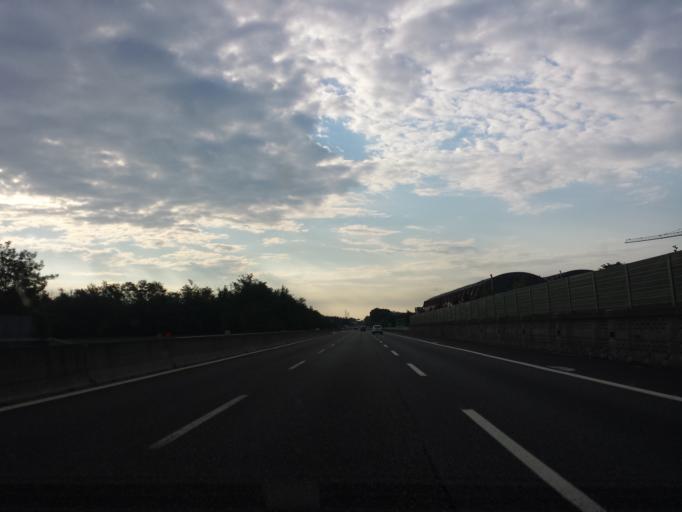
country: IT
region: Lombardy
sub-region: Provincia di Varese
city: Marnate
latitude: 45.6154
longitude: 8.9157
